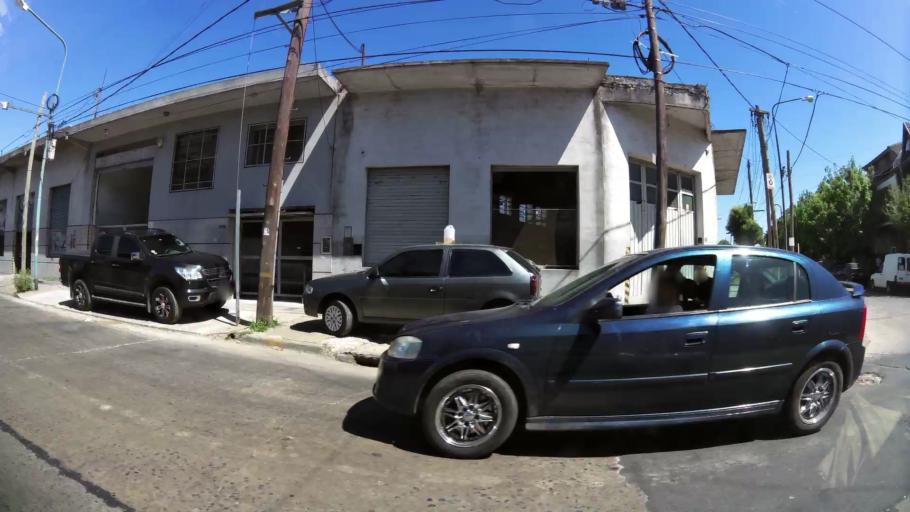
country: AR
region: Buenos Aires
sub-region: Partido de General San Martin
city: General San Martin
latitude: -34.5438
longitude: -58.5375
